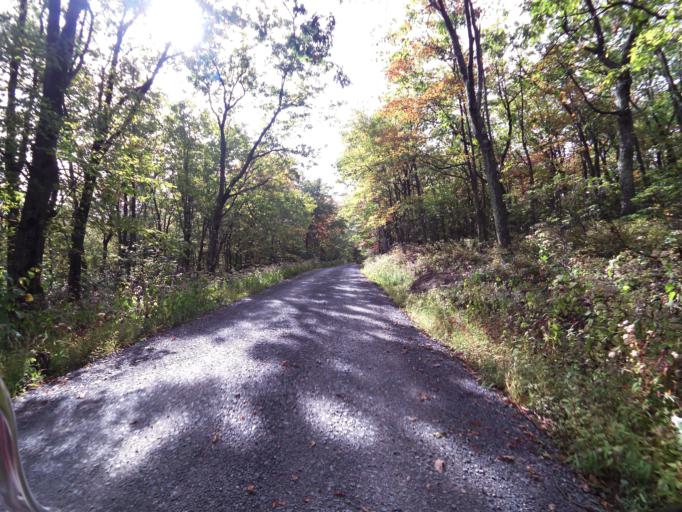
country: US
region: Pennsylvania
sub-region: Lycoming County
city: Duboistown
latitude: 41.1125
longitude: -77.1392
